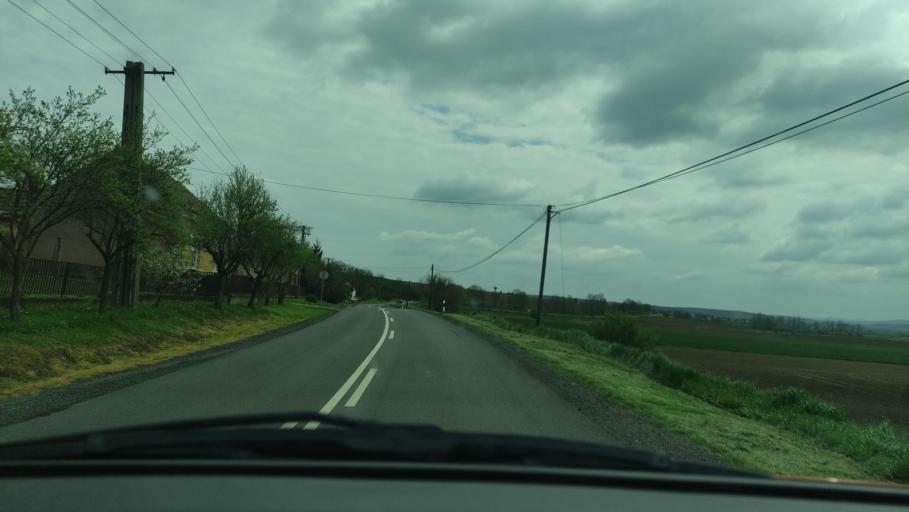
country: HU
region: Baranya
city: Sasd
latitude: 46.2647
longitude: 18.0847
